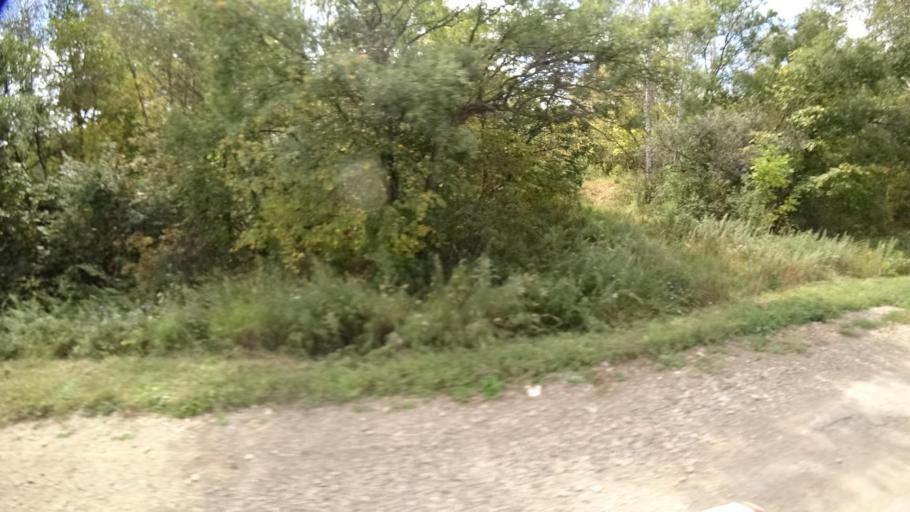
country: RU
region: Primorskiy
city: Yakovlevka
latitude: 44.7101
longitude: 133.6318
